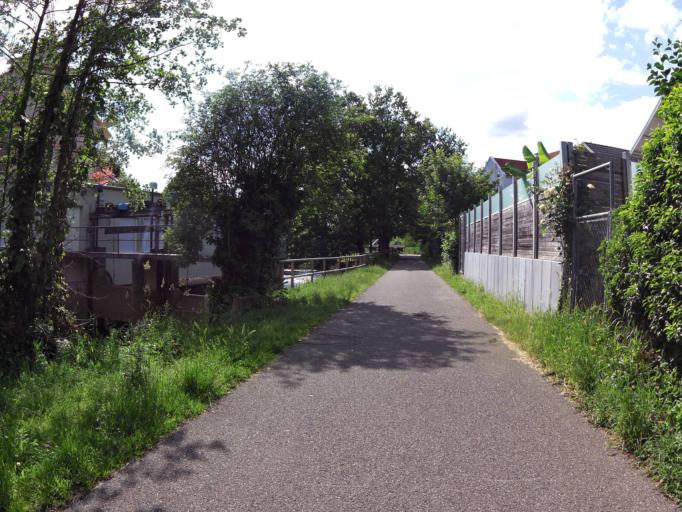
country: DE
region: Baden-Wuerttemberg
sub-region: Freiburg Region
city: Lahr
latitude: 48.3381
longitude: 7.8553
